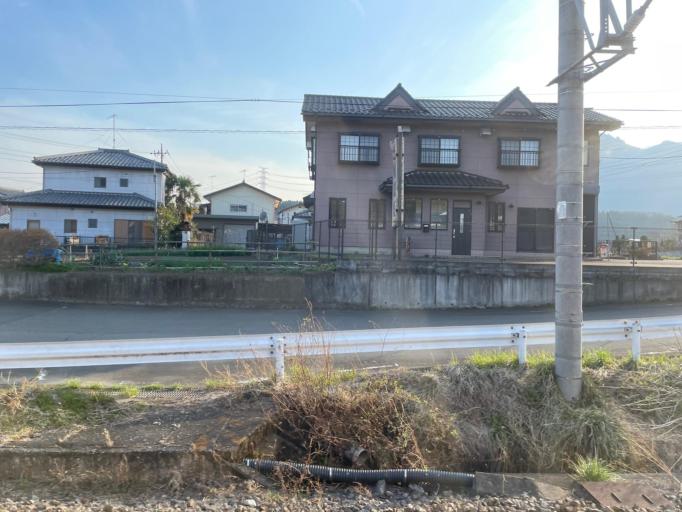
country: JP
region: Gunma
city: Annaka
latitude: 36.3156
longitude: 138.7876
